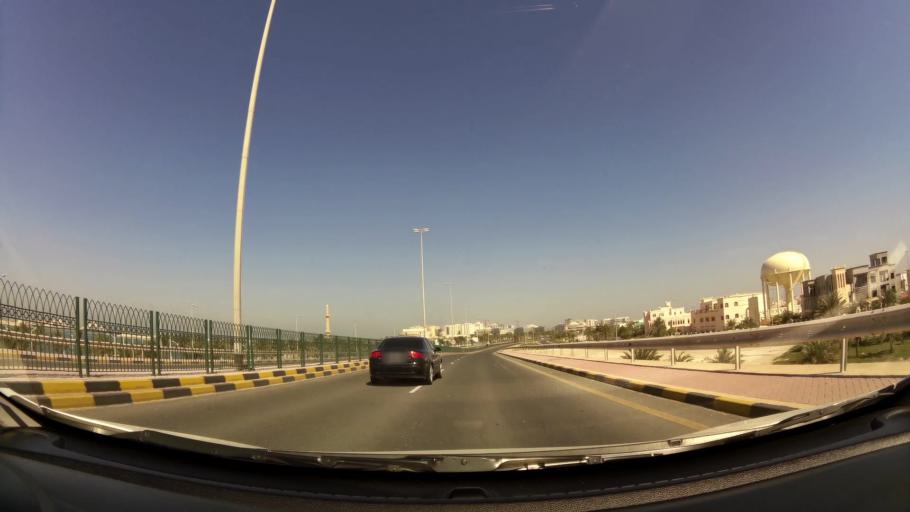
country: BH
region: Muharraq
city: Al Muharraq
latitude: 26.2516
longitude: 50.6046
